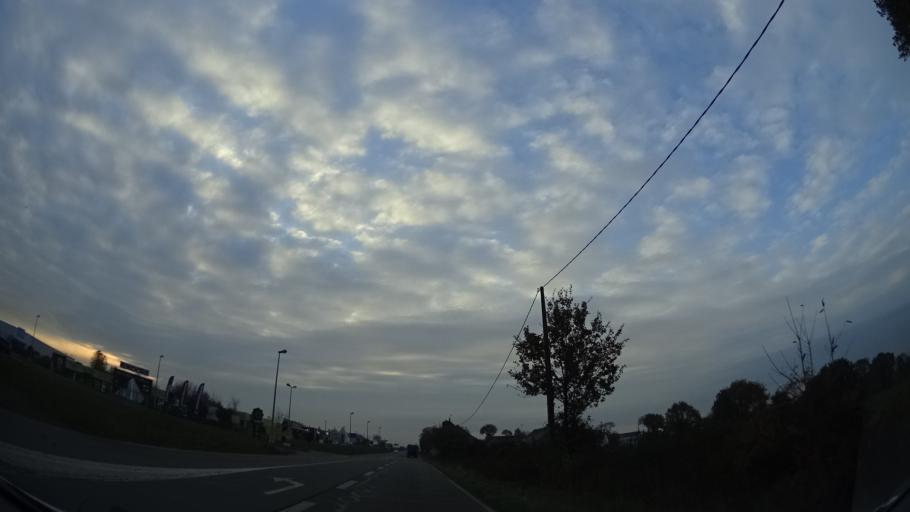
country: FR
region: Brittany
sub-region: Departement d'Ille-et-Vilaine
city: La Chapelle-des-Fougeretz
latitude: 48.1869
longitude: -1.7263
